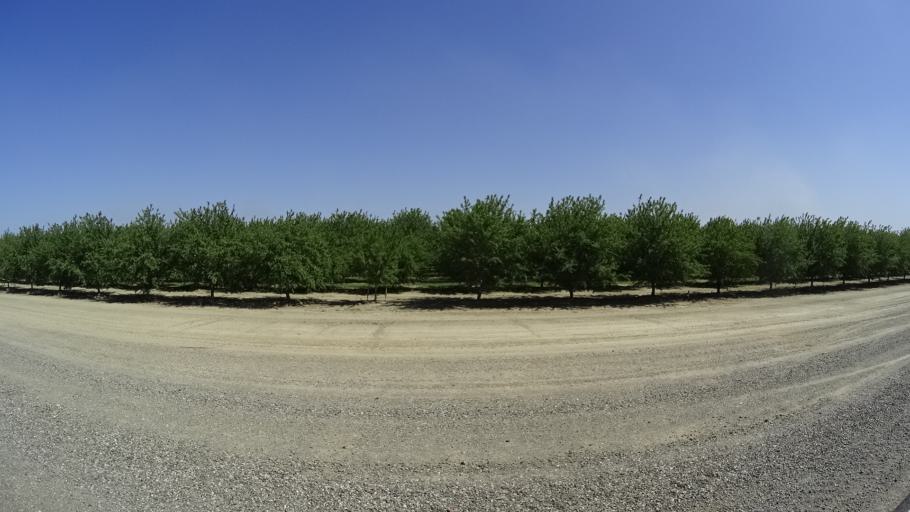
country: US
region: California
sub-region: Glenn County
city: Willows
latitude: 39.5850
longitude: -122.1371
